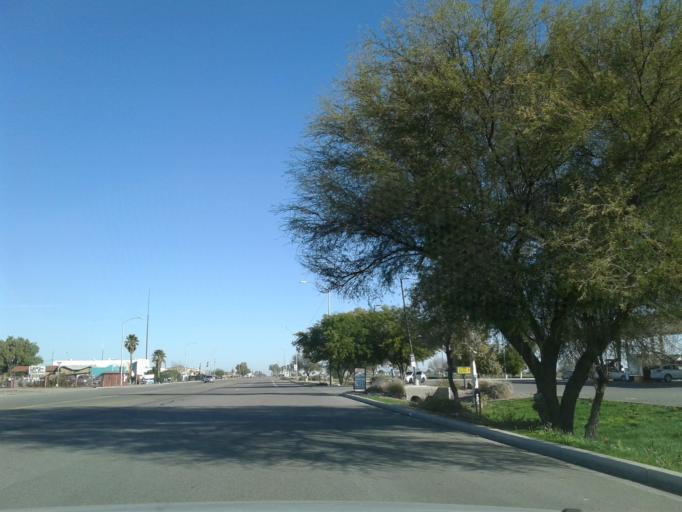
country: US
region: Arizona
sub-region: Pinal County
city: Eloy
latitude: 32.7382
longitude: -111.5503
